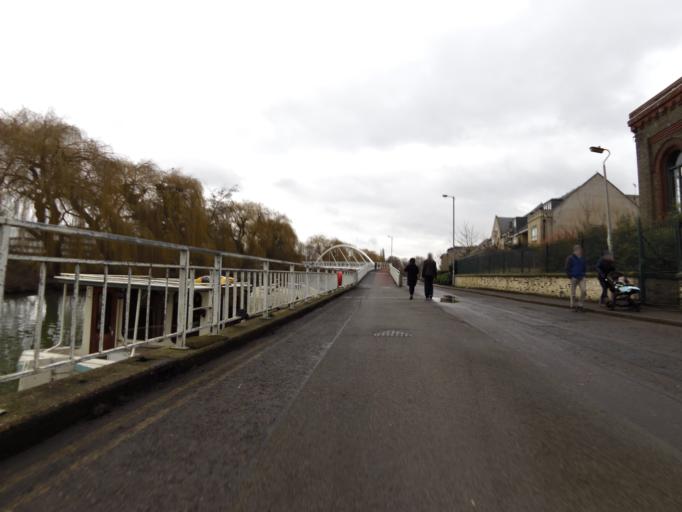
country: GB
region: England
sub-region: Cambridgeshire
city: Cambridge
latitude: 52.2127
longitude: 0.1427
